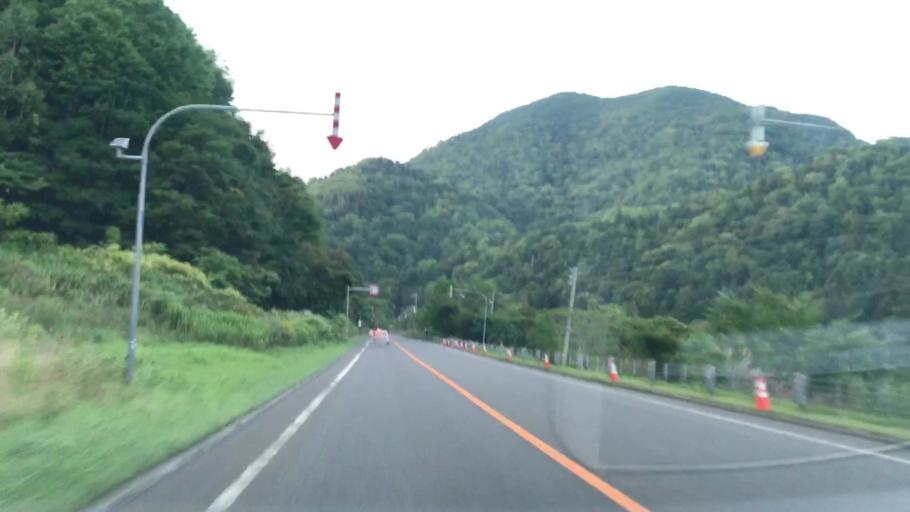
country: JP
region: Hokkaido
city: Sapporo
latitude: 42.9168
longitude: 141.1244
